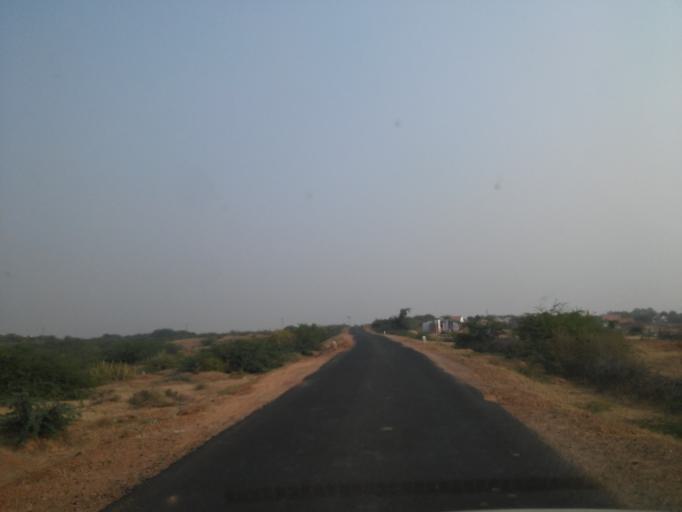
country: IN
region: Gujarat
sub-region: Kachchh
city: Bhuj
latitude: 23.8229
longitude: 69.7365
